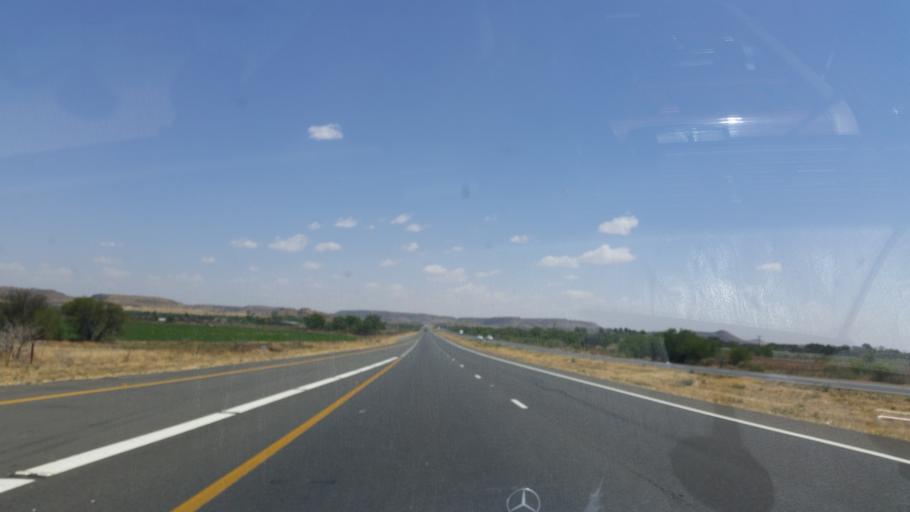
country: ZA
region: Orange Free State
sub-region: Mangaung Metropolitan Municipality
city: Bloemfontein
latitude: -28.9664
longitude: 26.3427
